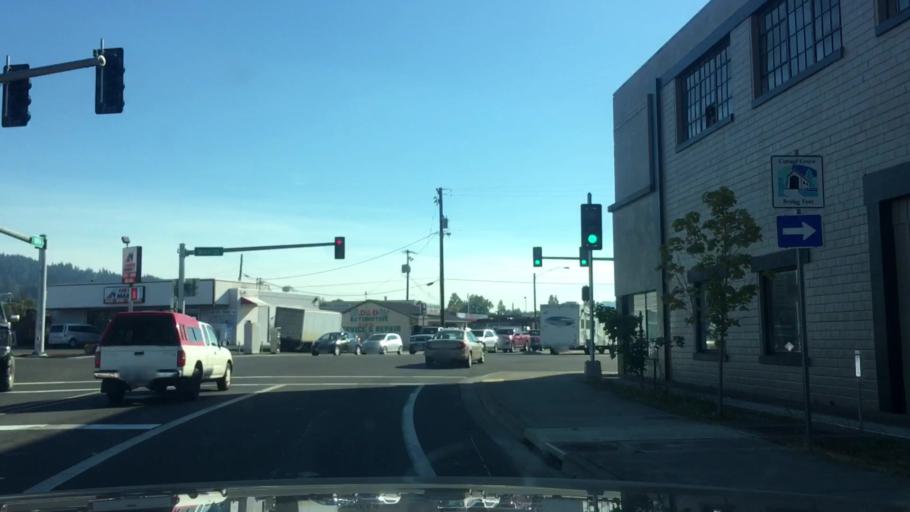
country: US
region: Oregon
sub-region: Lane County
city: Cottage Grove
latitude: 43.7976
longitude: -123.0591
